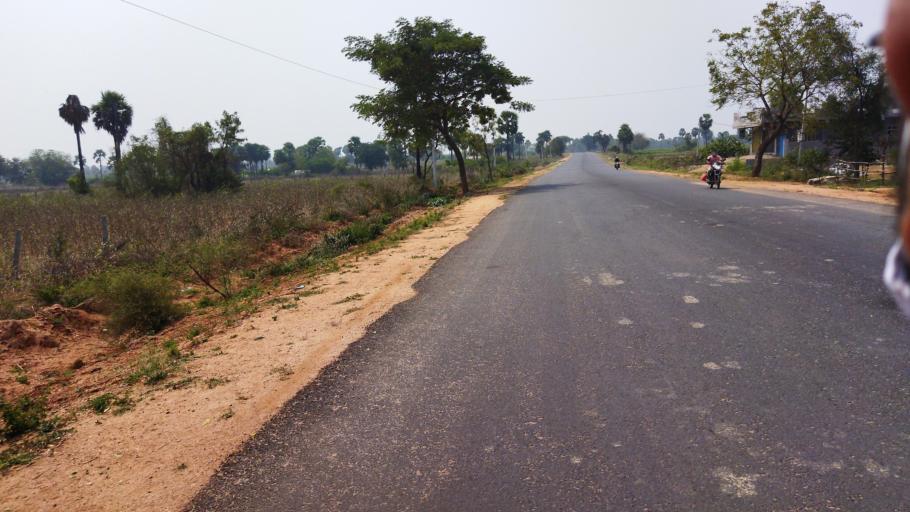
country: IN
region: Telangana
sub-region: Nalgonda
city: Nalgonda
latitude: 17.1565
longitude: 79.4136
